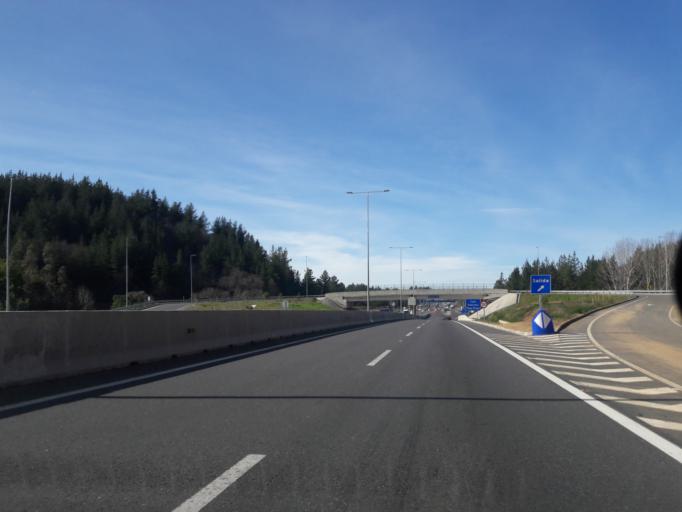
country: CL
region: Biobio
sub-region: Provincia de Biobio
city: Yumbel
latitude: -36.9596
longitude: -72.7337
